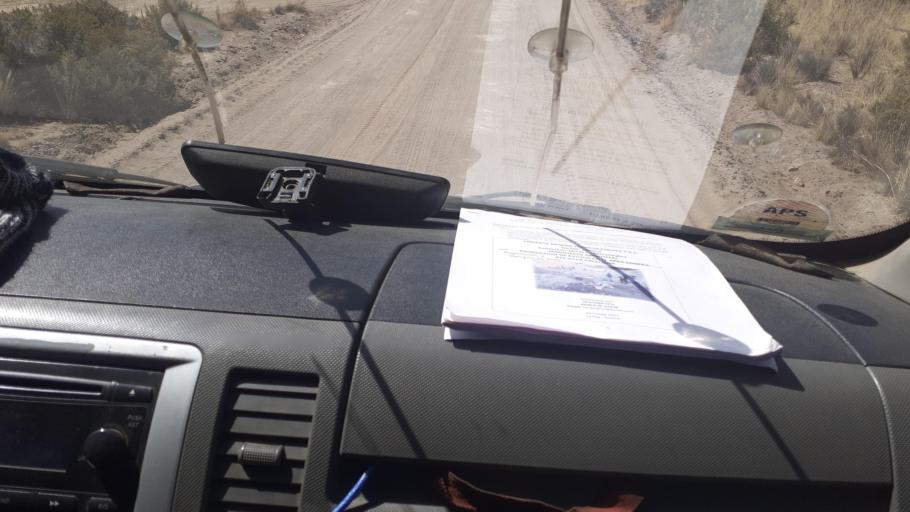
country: BO
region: La Paz
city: Tiahuanaco
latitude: -17.1097
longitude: -68.8080
